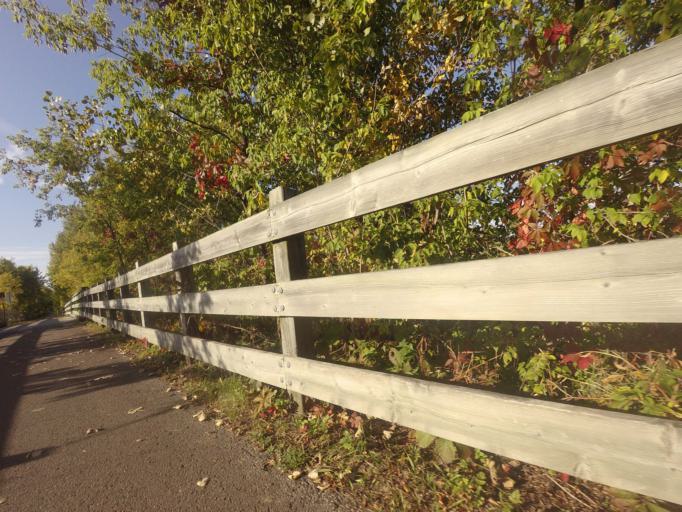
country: CA
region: Quebec
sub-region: Laurentides
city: Saint-Jerome
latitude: 45.7324
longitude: -73.9459
